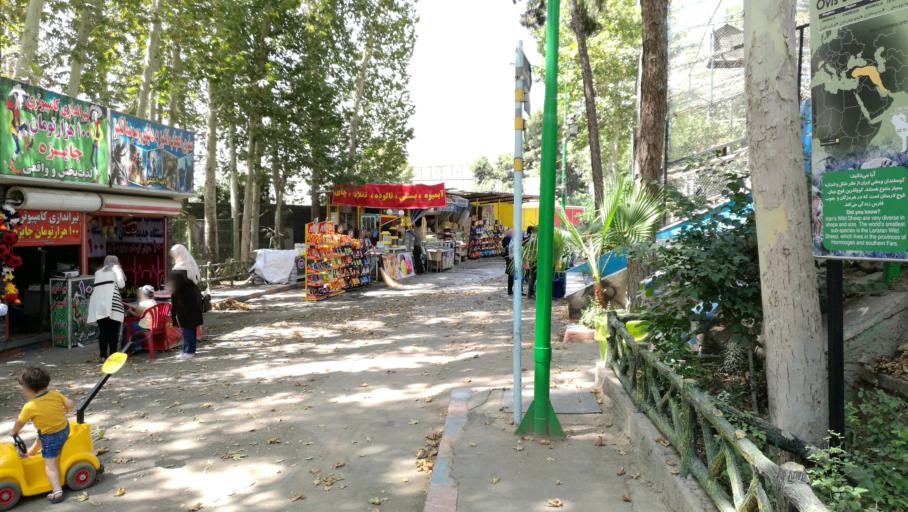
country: IR
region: Tehran
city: Tehran
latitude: 35.7178
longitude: 51.2948
